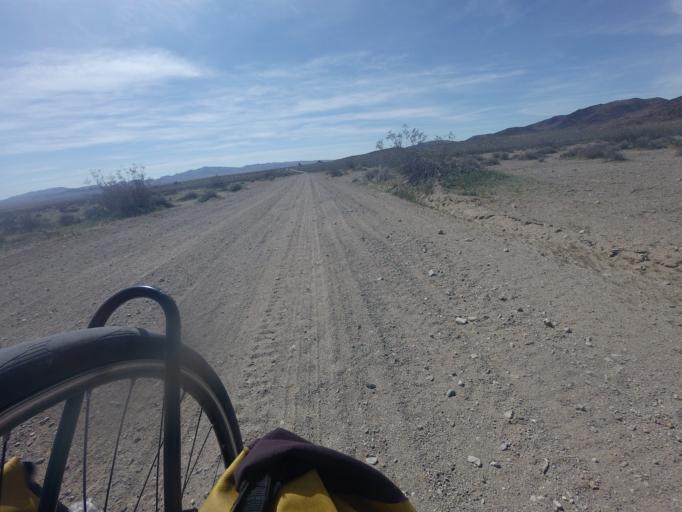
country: US
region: California
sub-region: San Bernardino County
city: Searles Valley
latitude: 35.5833
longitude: -117.4249
